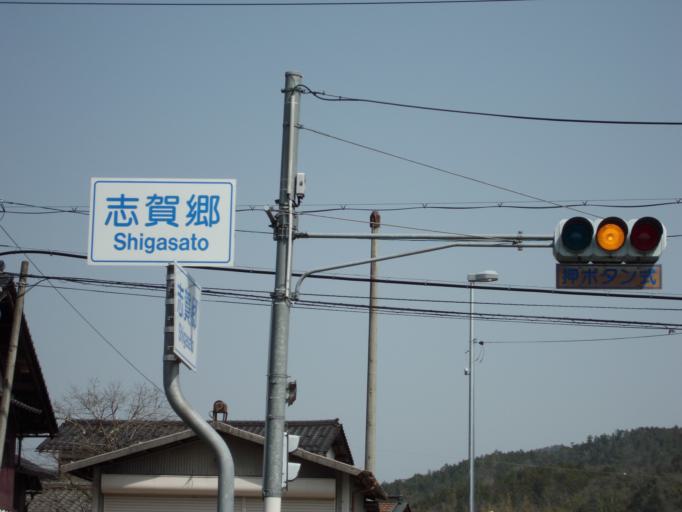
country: JP
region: Kyoto
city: Ayabe
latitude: 35.3678
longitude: 135.2398
